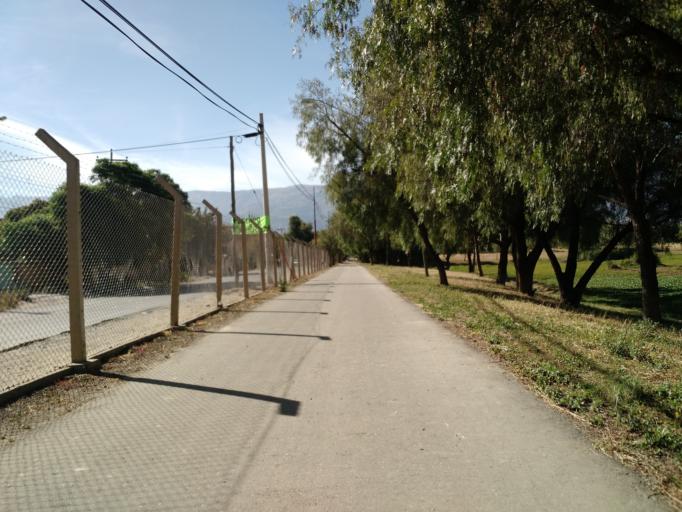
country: BO
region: Cochabamba
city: Cochabamba
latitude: -17.3879
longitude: -66.2078
